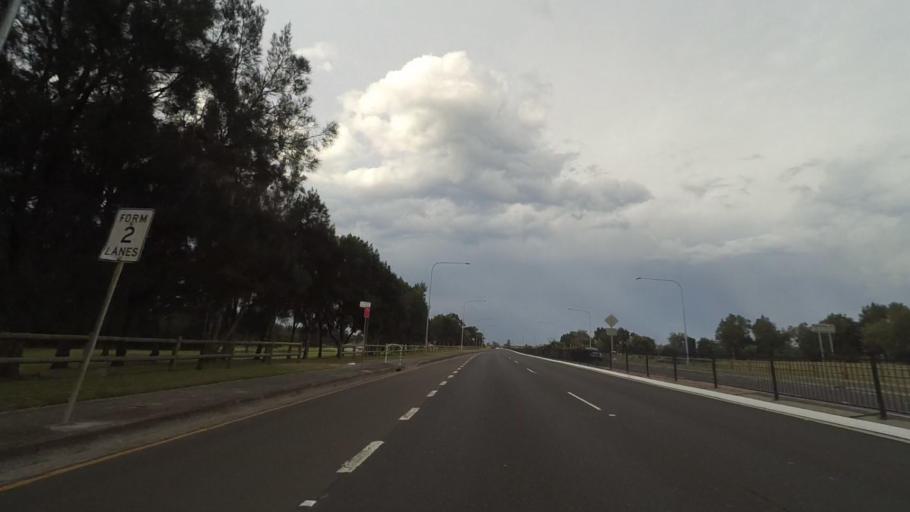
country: AU
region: New South Wales
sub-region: Shellharbour
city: Lake Illawarra
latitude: -34.5395
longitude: 150.8650
